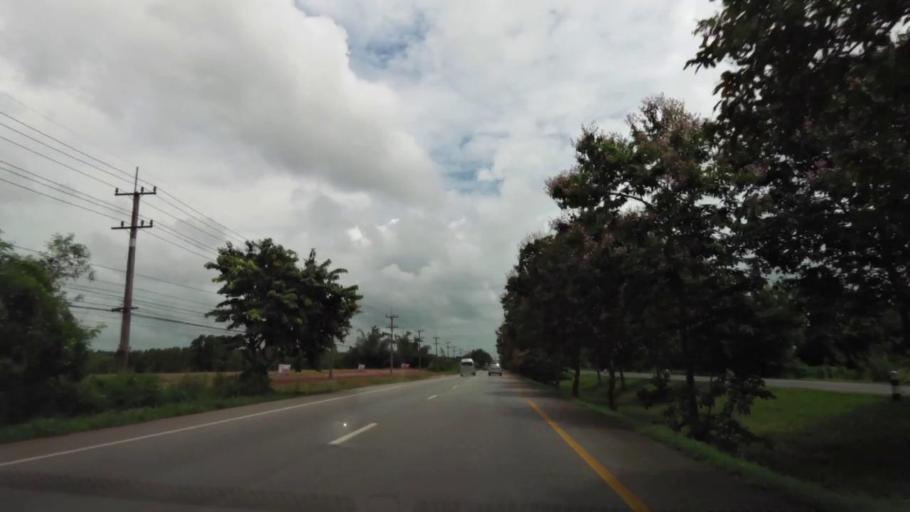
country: TH
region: Chanthaburi
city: Na Yai Am
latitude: 12.7495
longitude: 101.8740
